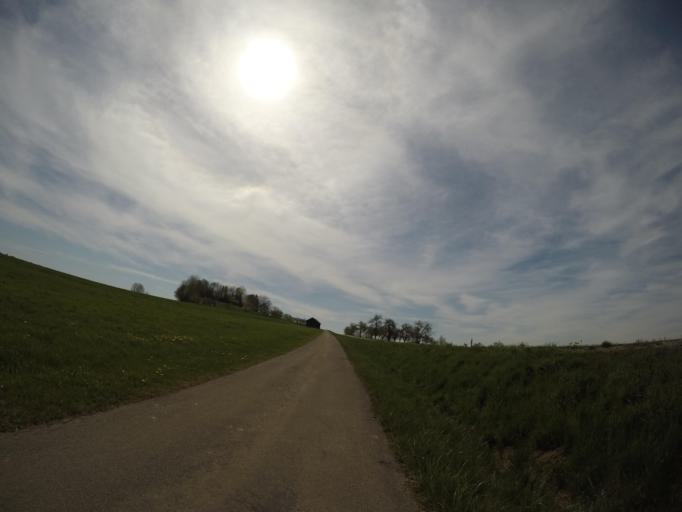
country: DE
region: Baden-Wuerttemberg
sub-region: Tuebingen Region
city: Altshausen
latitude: 47.9434
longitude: 9.5296
